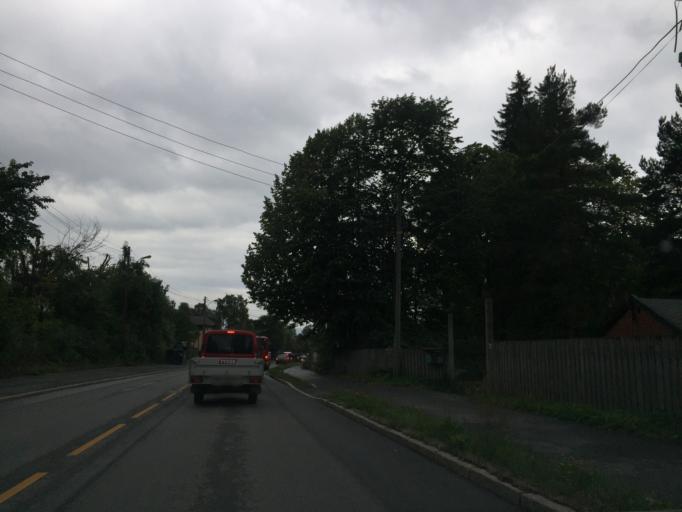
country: NO
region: Oslo
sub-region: Oslo
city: Sjolyststranda
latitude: 59.9429
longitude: 10.6814
